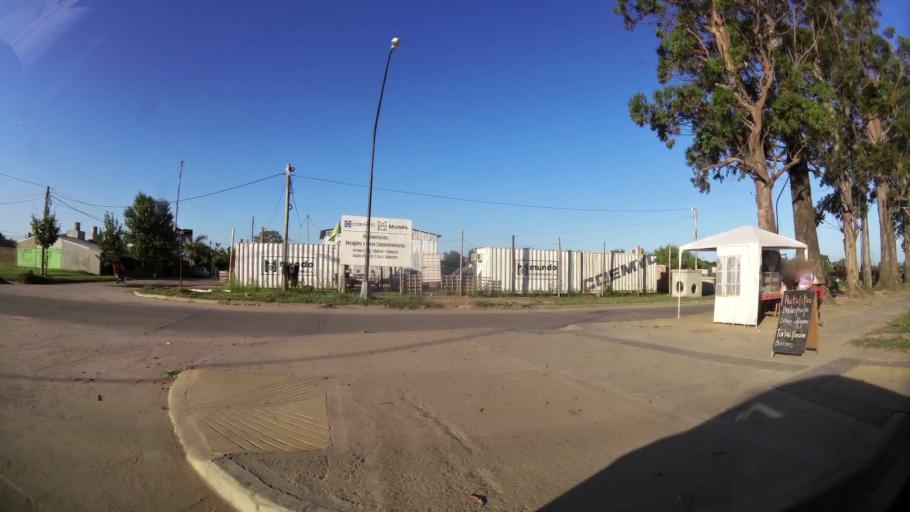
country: AR
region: Santa Fe
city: Santa Fe de la Vera Cruz
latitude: -31.5954
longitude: -60.6785
